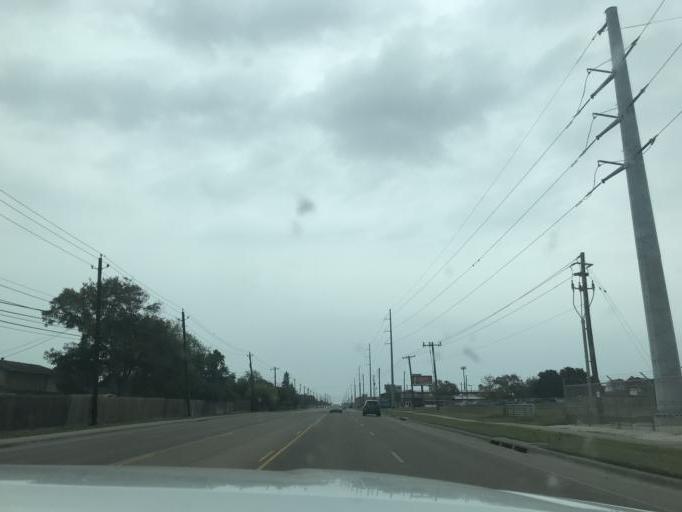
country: US
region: Texas
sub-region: Nueces County
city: Corpus Christi
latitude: 27.6966
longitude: -97.3727
